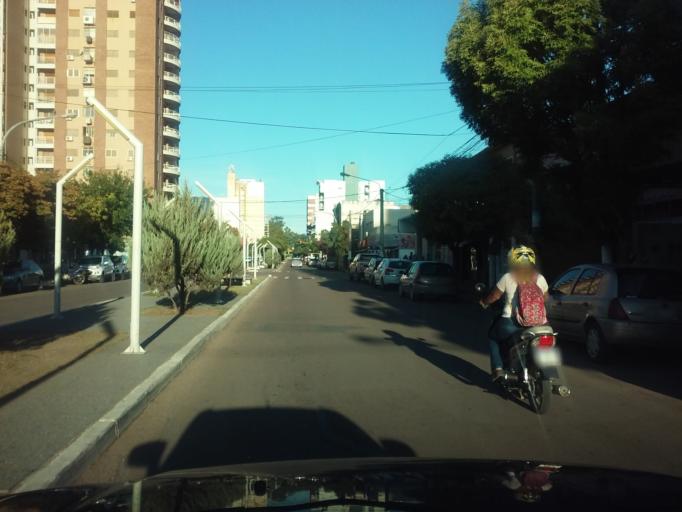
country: AR
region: La Pampa
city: Santa Rosa
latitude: -36.6210
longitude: -64.2866
